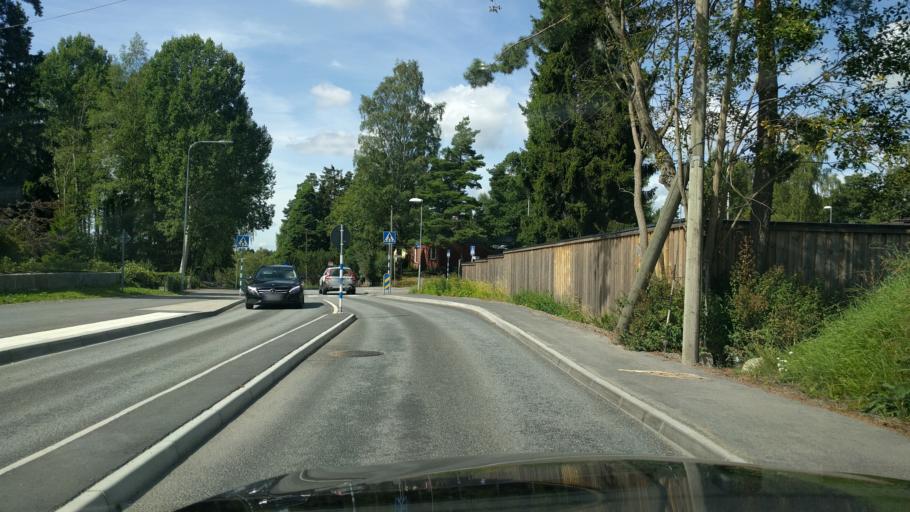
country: SE
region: Stockholm
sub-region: Taby Kommun
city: Taby
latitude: 59.4502
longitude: 18.0603
